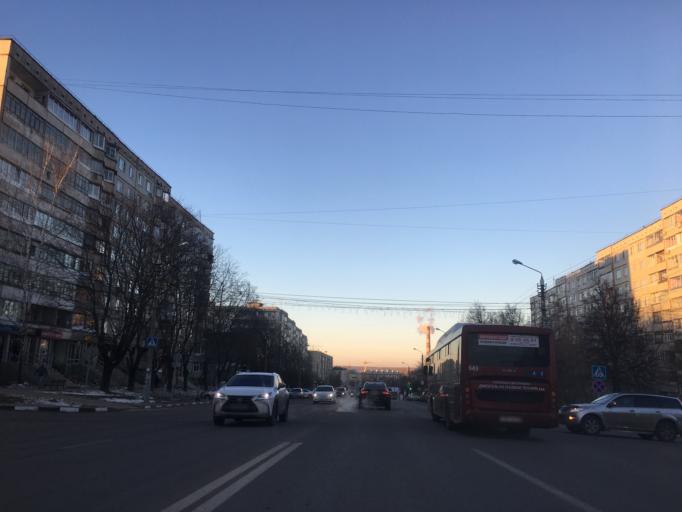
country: RU
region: Tula
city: Tula
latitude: 54.1926
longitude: 37.5914
